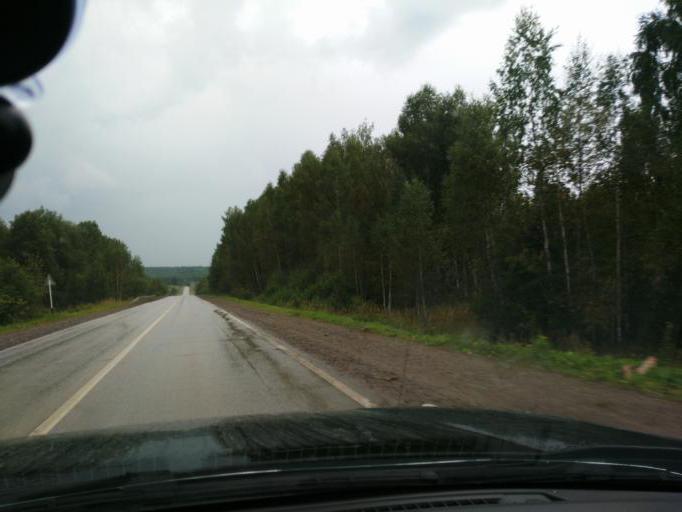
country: RU
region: Perm
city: Barda
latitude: 56.8852
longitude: 55.8277
